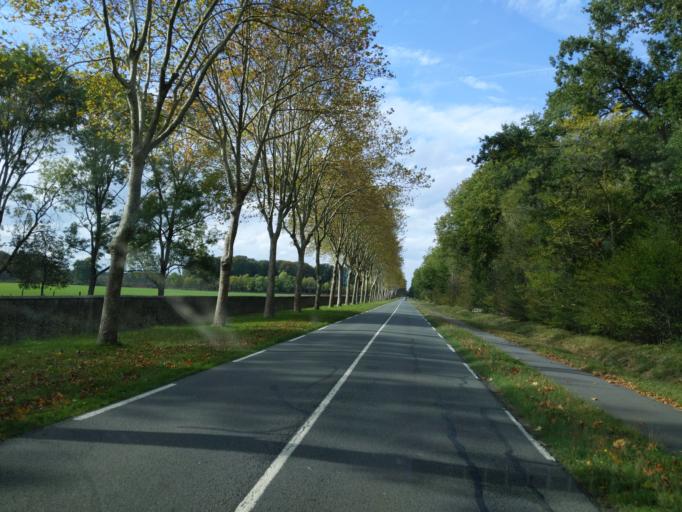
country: FR
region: Ile-de-France
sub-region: Departement des Yvelines
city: Rambouillet
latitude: 48.6619
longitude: 1.8141
